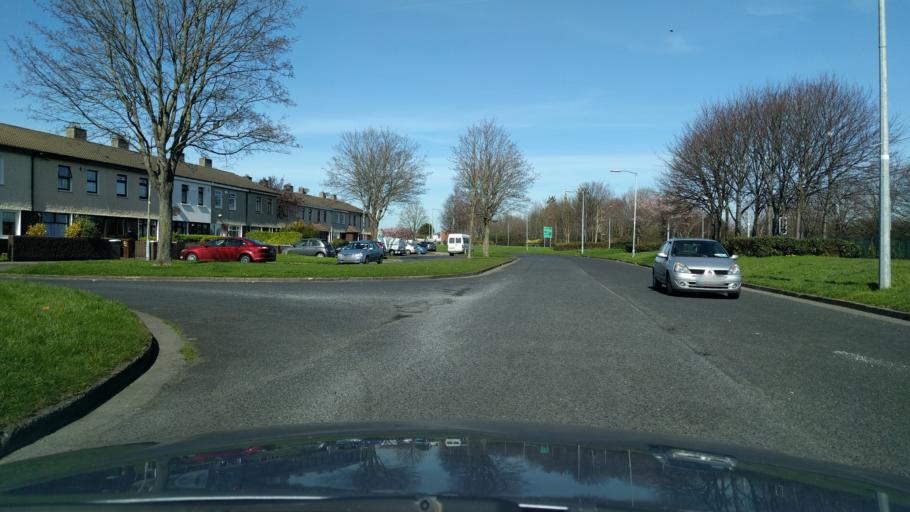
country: IE
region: Leinster
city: Tallaght
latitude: 53.2805
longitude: -6.3843
